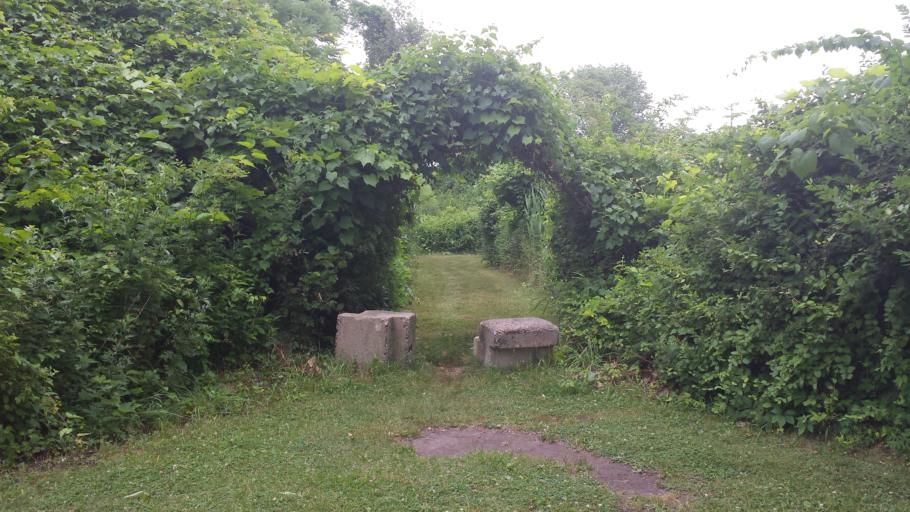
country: US
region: New York
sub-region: Westchester County
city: Montrose
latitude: 41.2365
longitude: -73.9427
